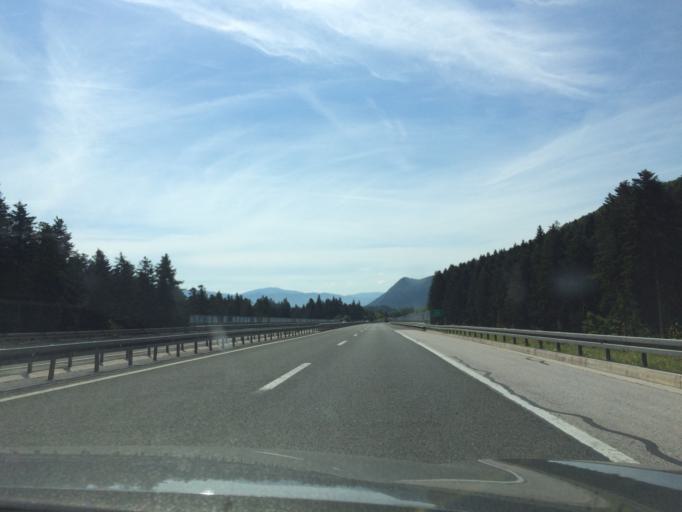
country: HR
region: Licko-Senjska
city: Otocac
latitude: 44.8476
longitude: 15.2350
